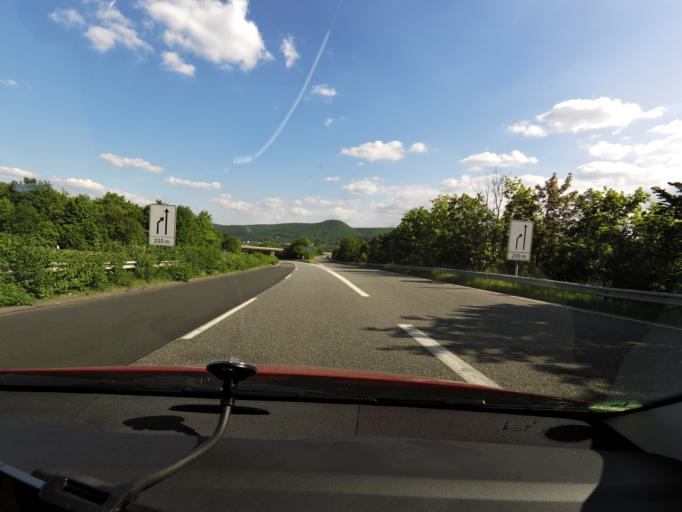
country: DE
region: Rheinland-Pfalz
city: Bad Neuenahr-Ahrweiler
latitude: 50.5540
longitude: 7.1179
